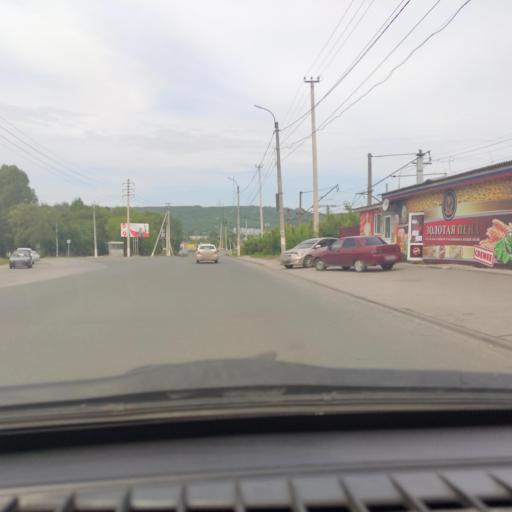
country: RU
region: Samara
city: Zhigulevsk
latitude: 53.4058
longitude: 49.4921
